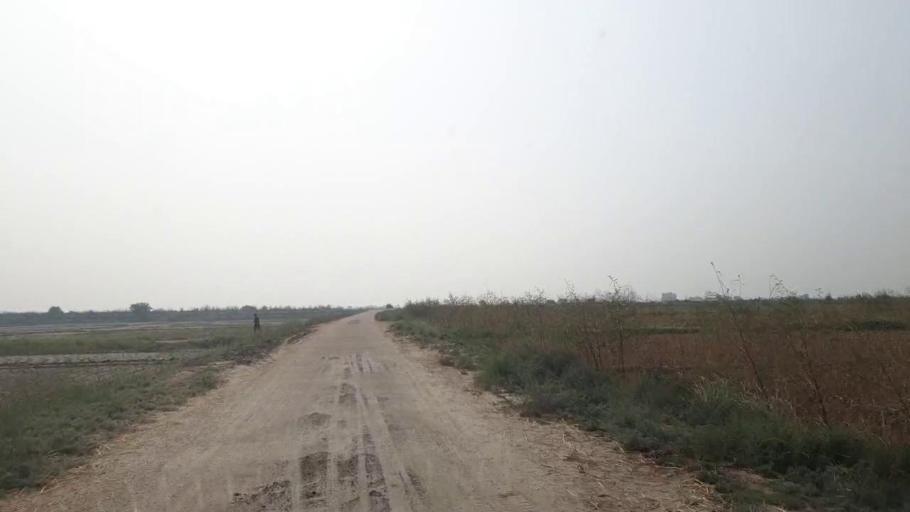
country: PK
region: Sindh
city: Matli
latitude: 25.1181
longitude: 68.6447
